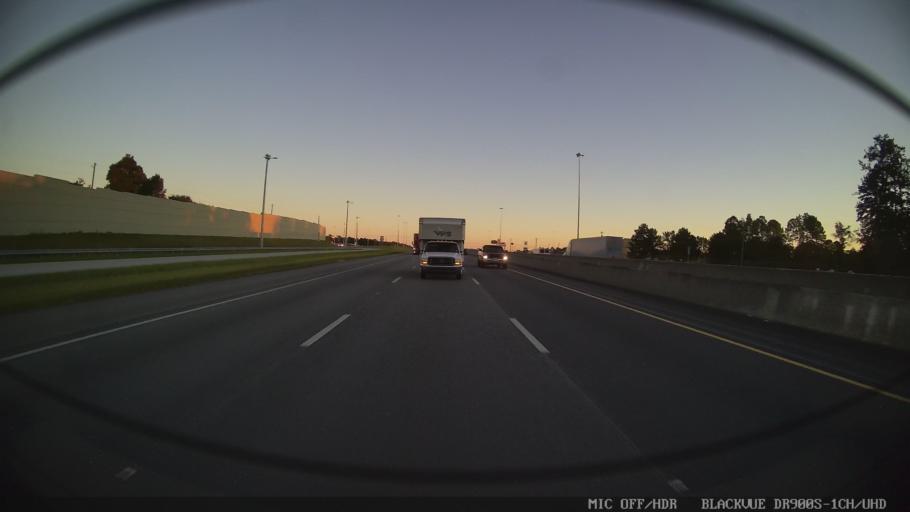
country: US
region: Georgia
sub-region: Lowndes County
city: Remerton
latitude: 30.8988
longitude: -83.3580
